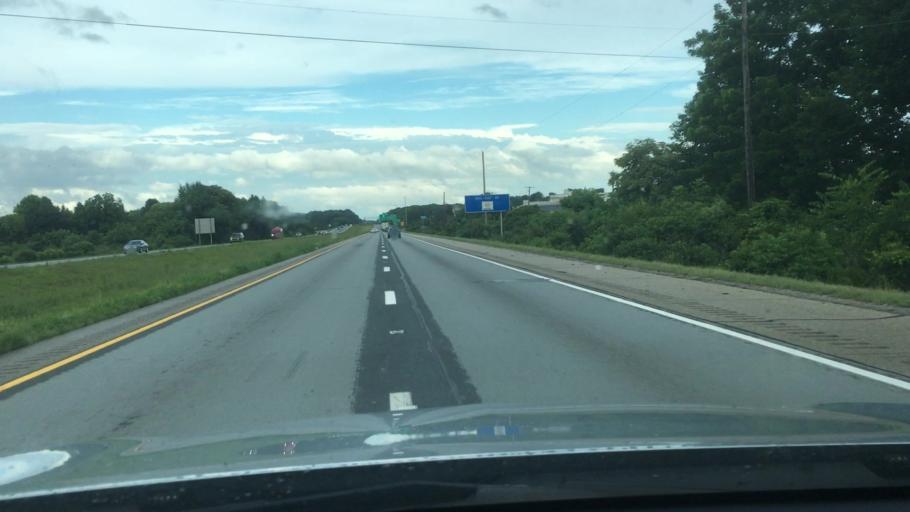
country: US
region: Pennsylvania
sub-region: Cumberland County
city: Carlisle
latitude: 40.1867
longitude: -77.2171
